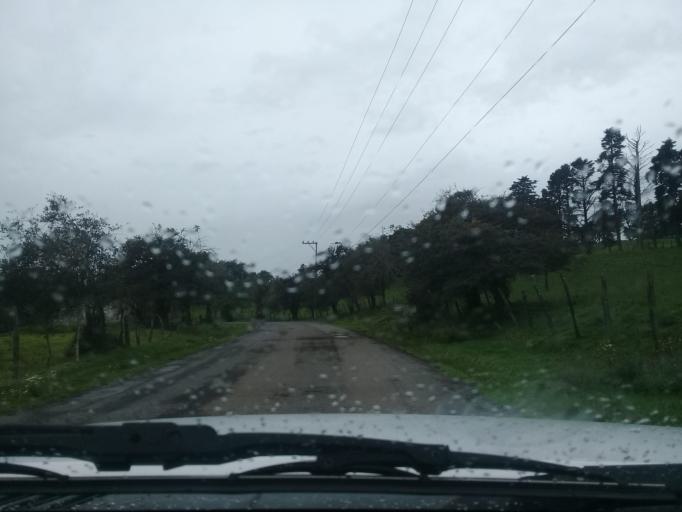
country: MX
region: Veracruz
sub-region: Acajete
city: La Joya
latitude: 19.6104
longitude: -97.0042
